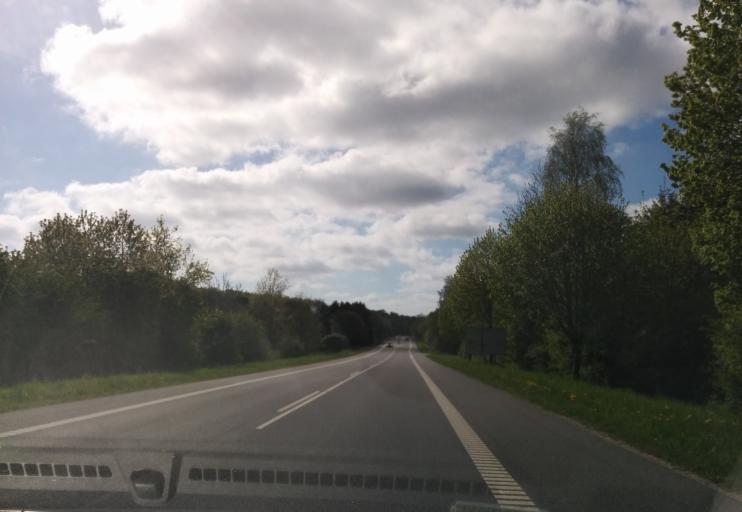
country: DK
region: South Denmark
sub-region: Assens Kommune
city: Vissenbjerg
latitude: 55.3914
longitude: 10.1214
